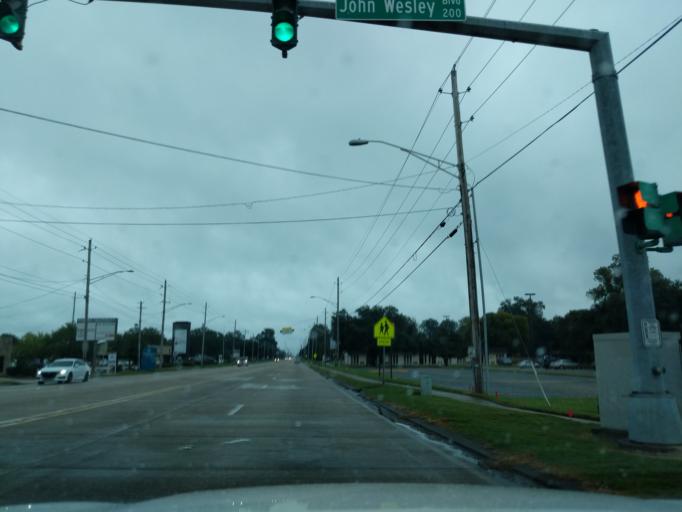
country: US
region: Louisiana
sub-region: Bossier Parish
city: Bossier City
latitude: 32.5184
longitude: -93.7070
